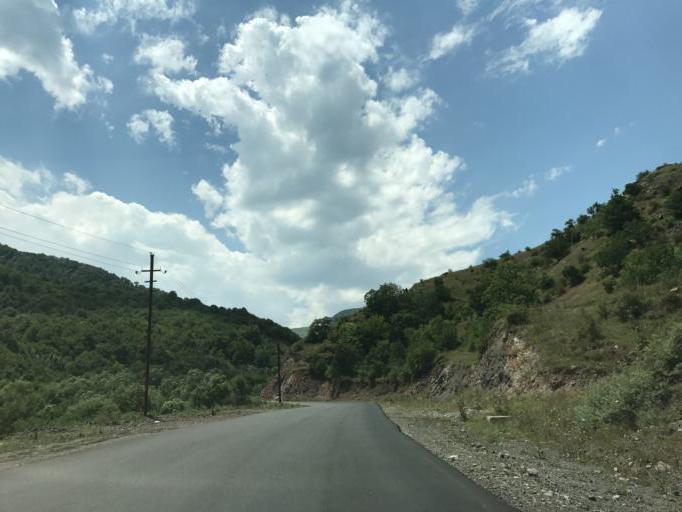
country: AZ
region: Kalbacar Rayonu
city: Kerbakhiar
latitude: 40.2319
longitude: 46.1103
